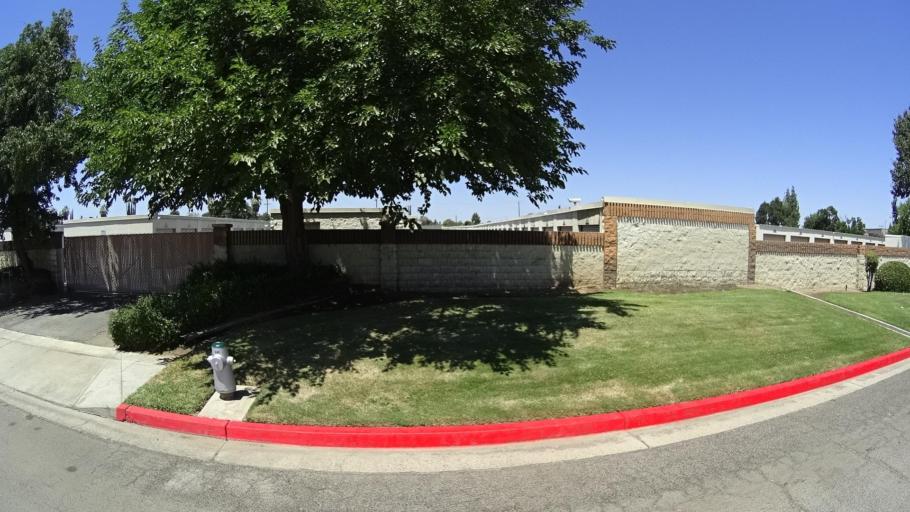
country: US
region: California
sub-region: Fresno County
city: Tarpey Village
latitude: 36.7762
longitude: -119.7301
